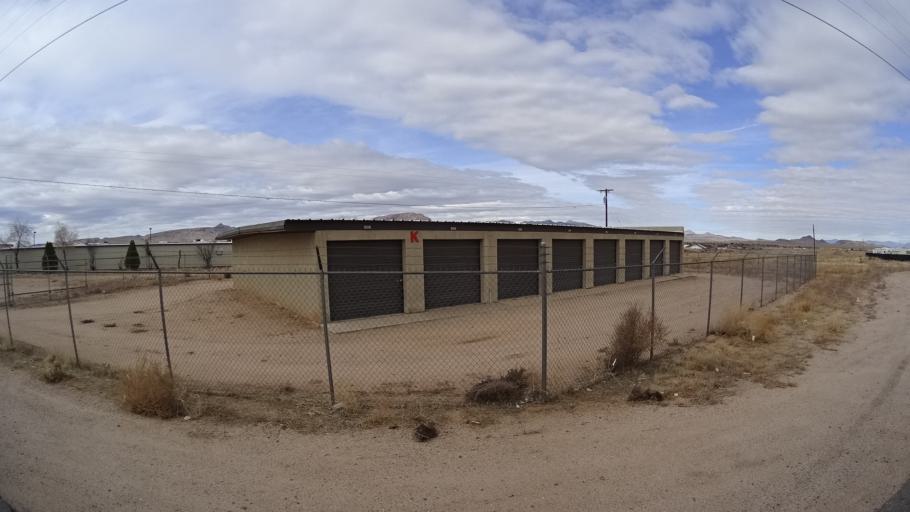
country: US
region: Arizona
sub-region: Mohave County
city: New Kingman-Butler
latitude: 35.2340
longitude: -113.9974
